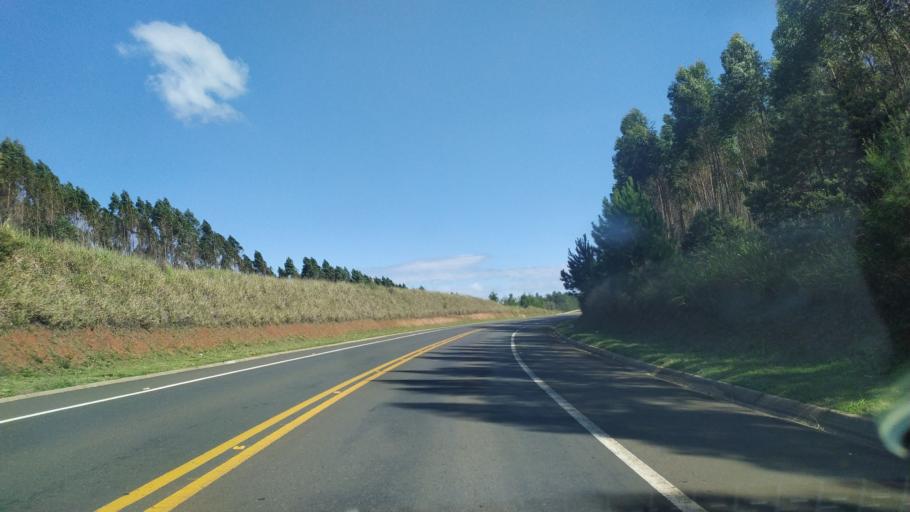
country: BR
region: Parana
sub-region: Telemaco Borba
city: Telemaco Borba
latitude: -24.2555
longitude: -50.7782
